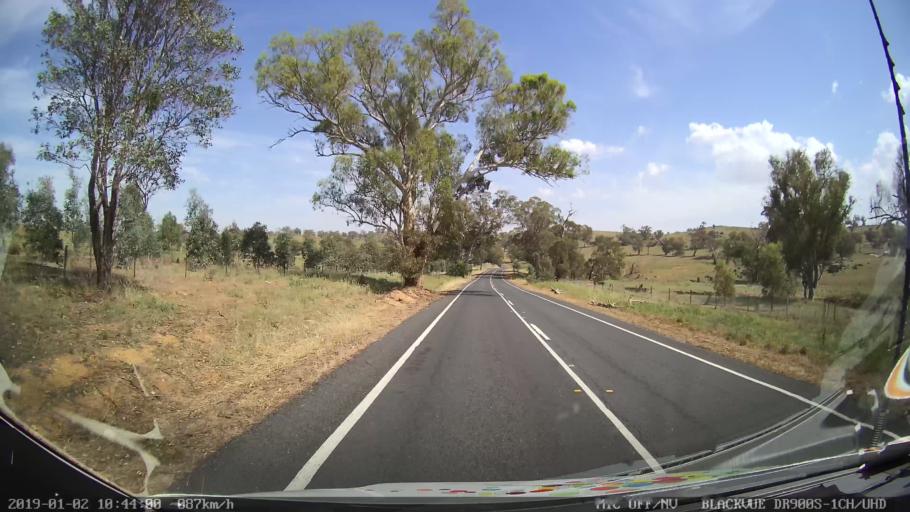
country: AU
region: New South Wales
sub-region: Cootamundra
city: Cootamundra
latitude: -34.7657
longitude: 148.2997
